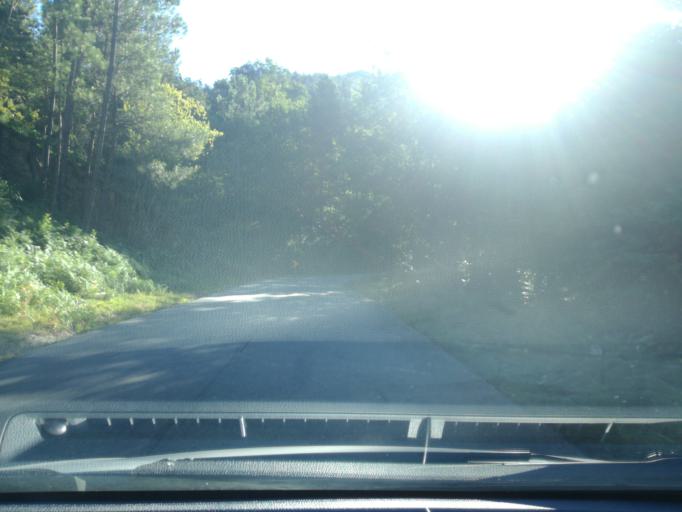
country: PT
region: Braga
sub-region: Vieira do Minho
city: Real
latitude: 41.7496
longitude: -8.1542
